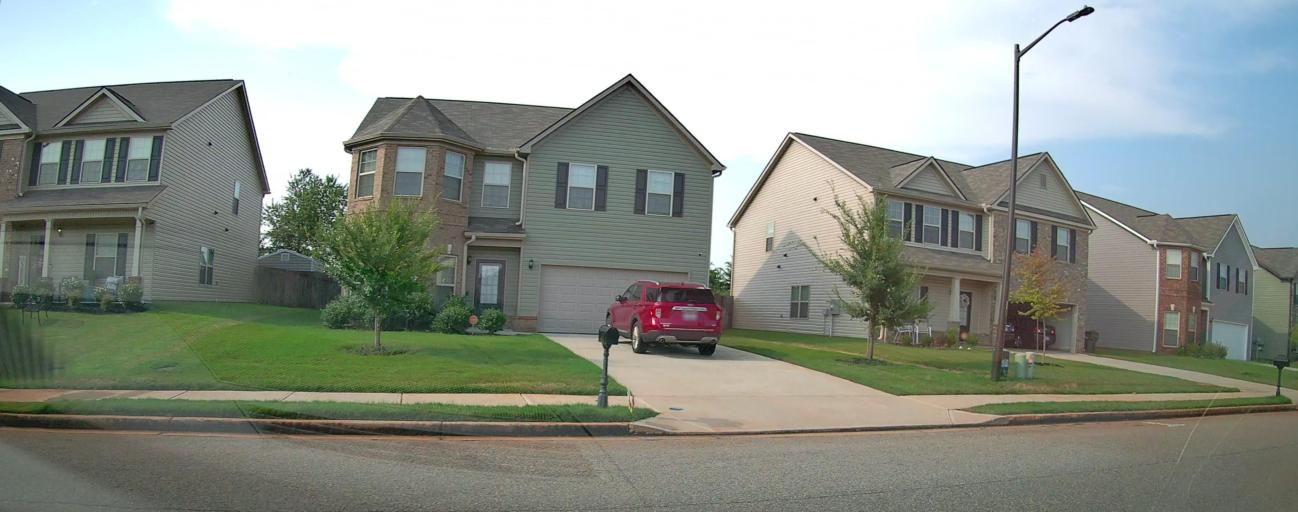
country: US
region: Georgia
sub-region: Houston County
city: Centerville
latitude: 32.6446
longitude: -83.7170
